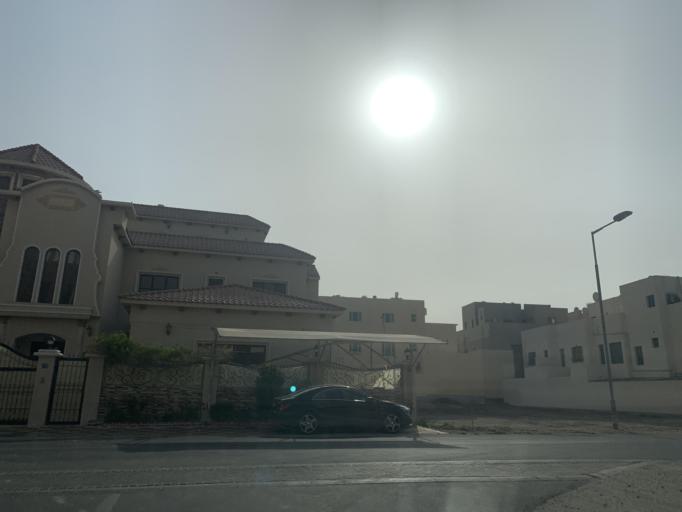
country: BH
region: Northern
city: Madinat `Isa
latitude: 26.1917
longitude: 50.5599
